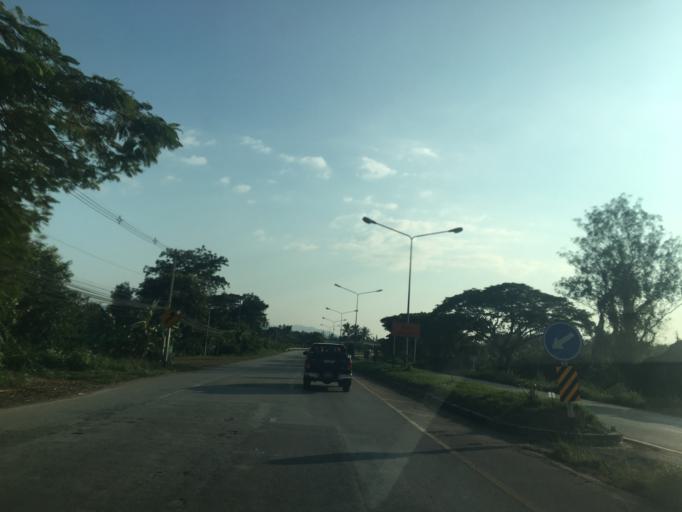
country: TH
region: Lampang
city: Ngao
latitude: 18.7382
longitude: 99.9741
